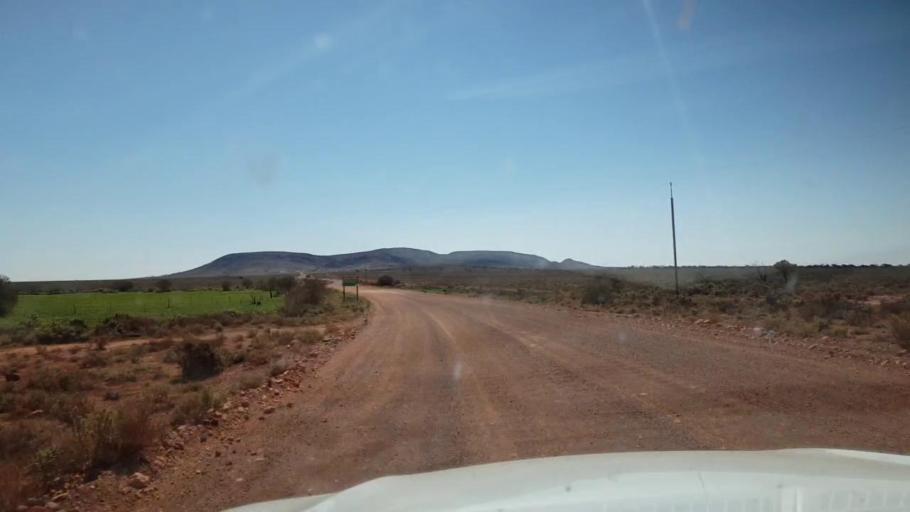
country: AU
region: South Australia
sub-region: Whyalla
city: Whyalla
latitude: -32.7162
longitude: 137.1433
